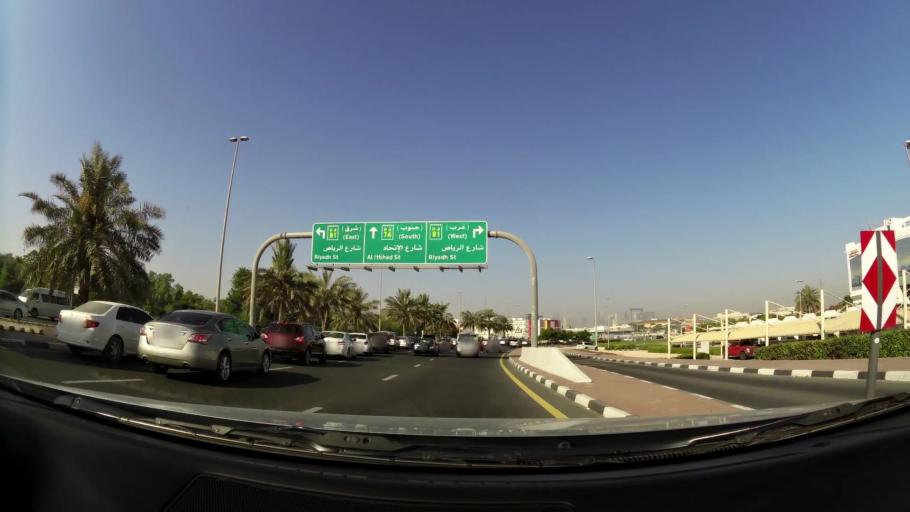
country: AE
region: Ash Shariqah
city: Sharjah
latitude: 25.2471
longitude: 55.3236
